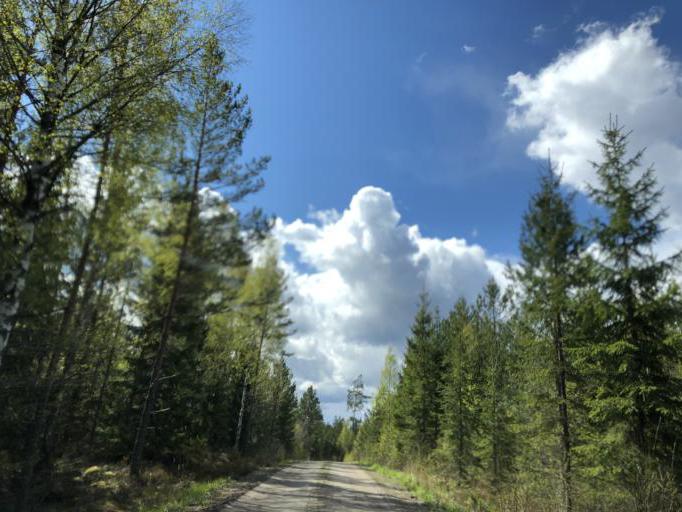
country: SE
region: Uppsala
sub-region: Heby Kommun
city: Tarnsjo
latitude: 60.2541
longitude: 16.9077
